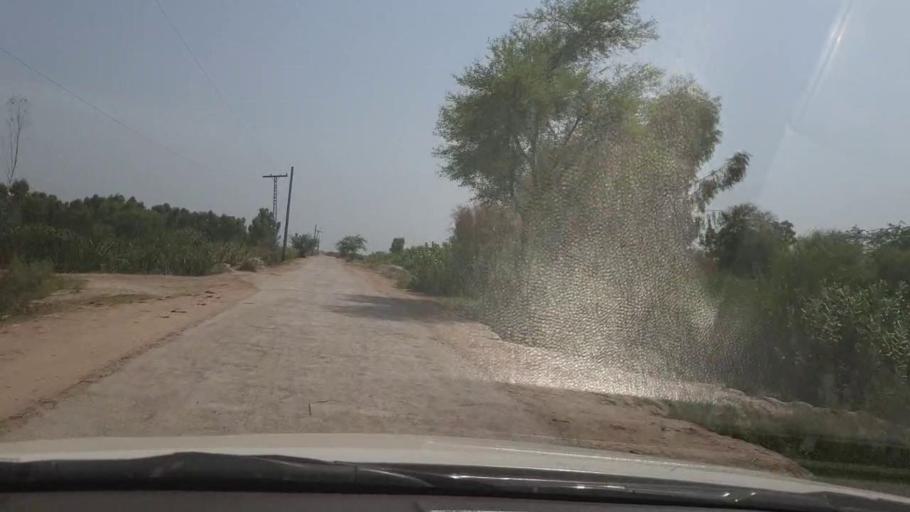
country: PK
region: Sindh
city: Garhi Yasin
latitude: 27.9701
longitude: 68.5038
